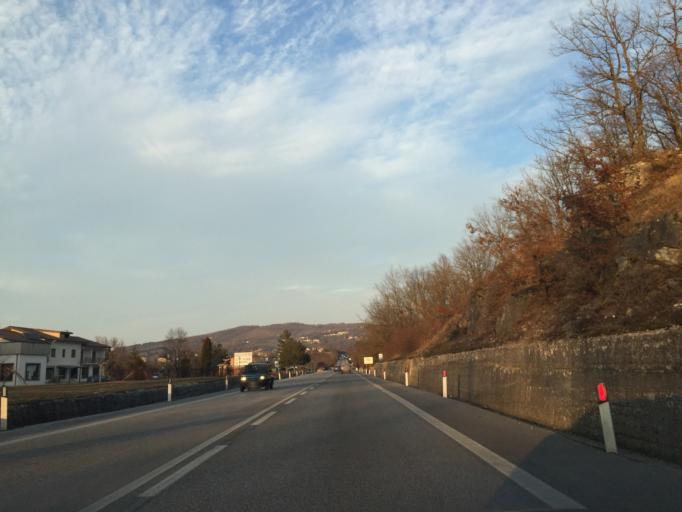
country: IT
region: Molise
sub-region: Provincia di Campobasso
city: Vinchiaturo
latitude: 41.4850
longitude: 14.5905
